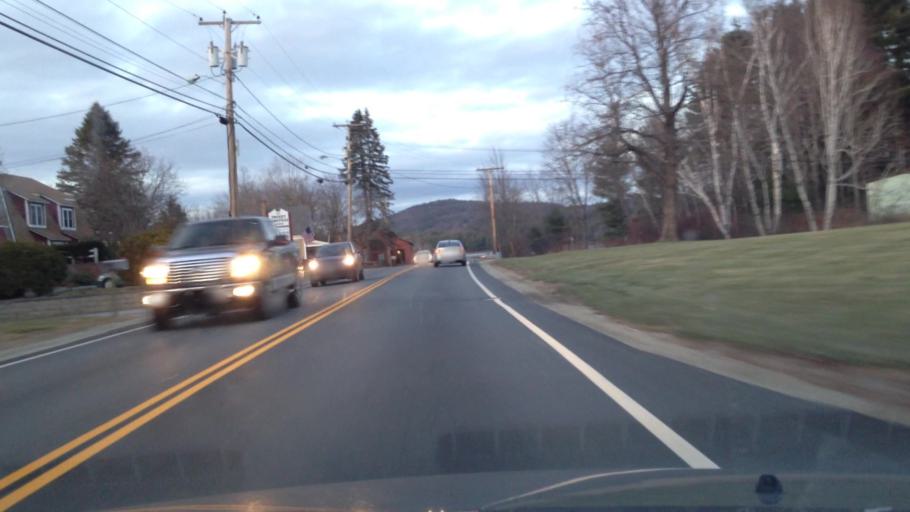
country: US
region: New Hampshire
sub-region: Cheshire County
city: Swanzey
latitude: 42.8958
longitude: -72.2639
